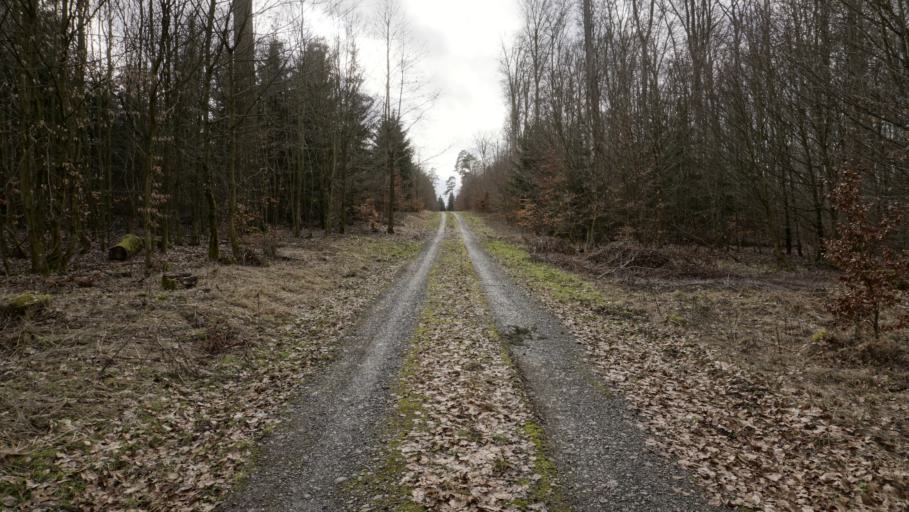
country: DE
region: Baden-Wuerttemberg
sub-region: Karlsruhe Region
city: Neckargerach
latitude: 49.4096
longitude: 9.1092
